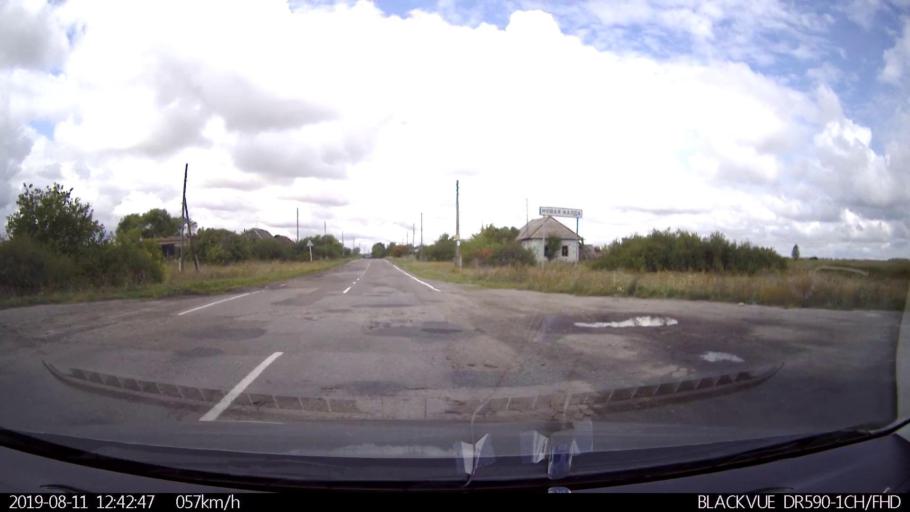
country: RU
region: Ulyanovsk
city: Ignatovka
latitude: 53.8482
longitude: 47.7477
